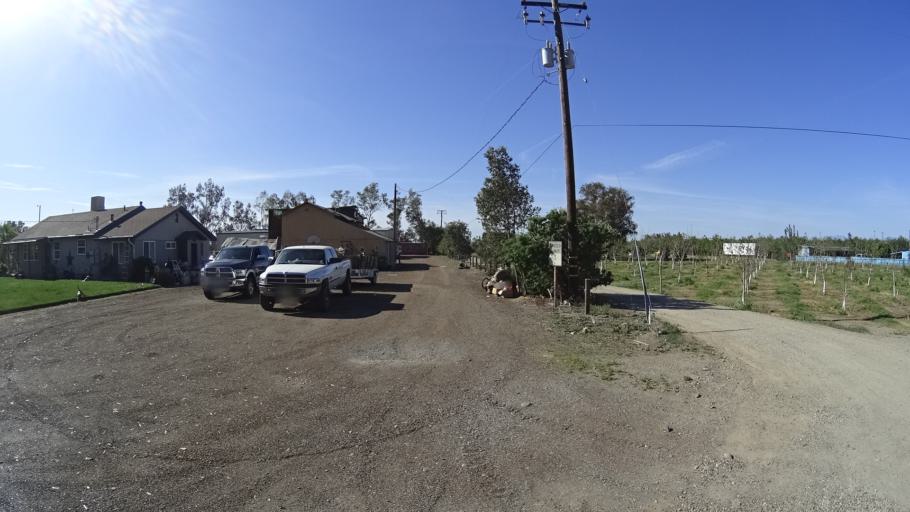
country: US
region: California
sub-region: Glenn County
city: Orland
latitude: 39.7113
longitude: -122.2020
